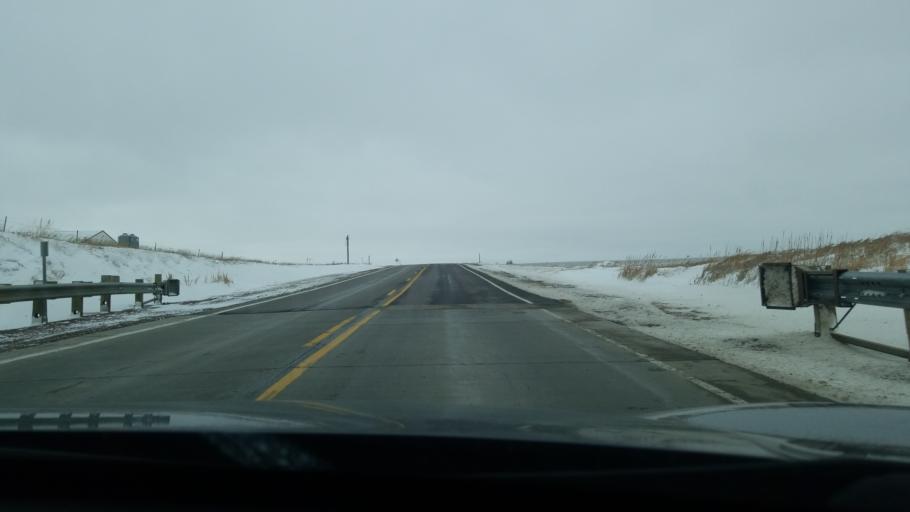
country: US
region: Iowa
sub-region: Sioux County
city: Hull
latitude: 43.2206
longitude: -96.1773
